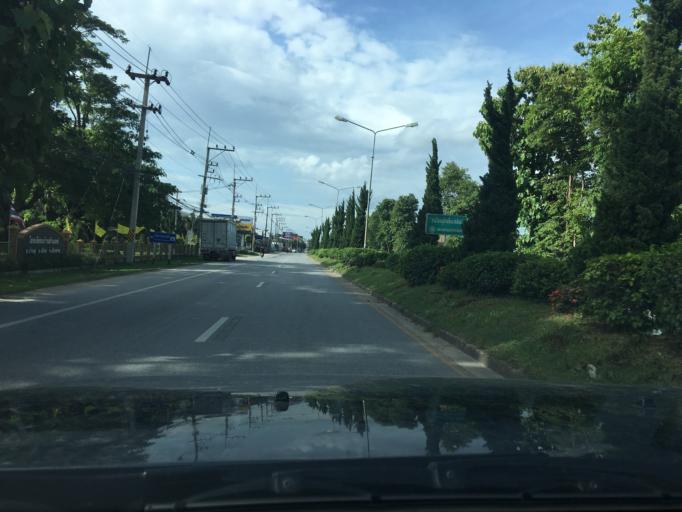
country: TH
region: Chiang Rai
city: Chiang Rai
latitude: 19.9479
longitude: 99.8479
